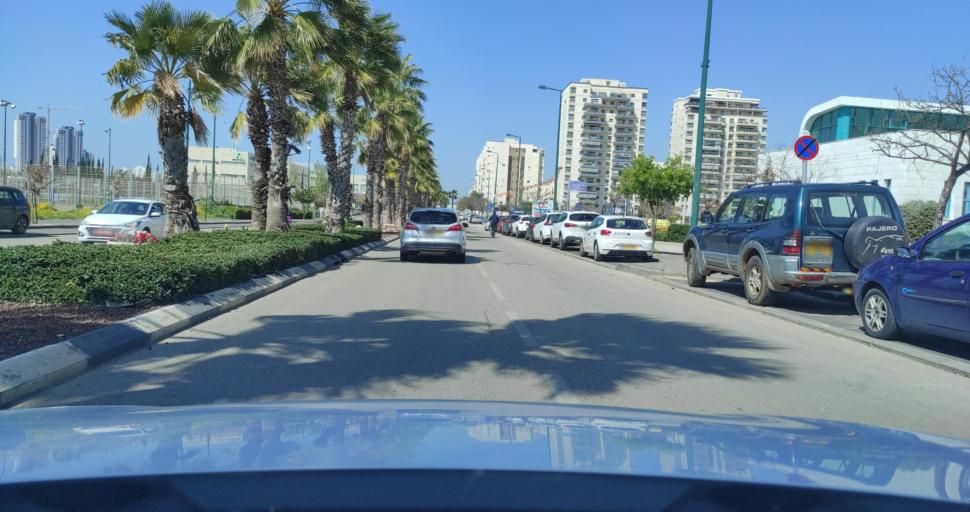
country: IL
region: Central District
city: Nordiyya
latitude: 32.3040
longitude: 34.8696
